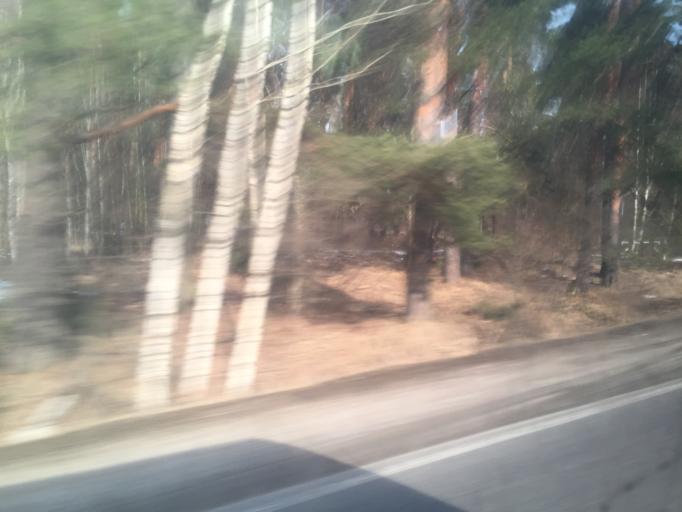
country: RU
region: Ivanovo
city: Lezhnevo
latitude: 56.8297
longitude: 40.8933
